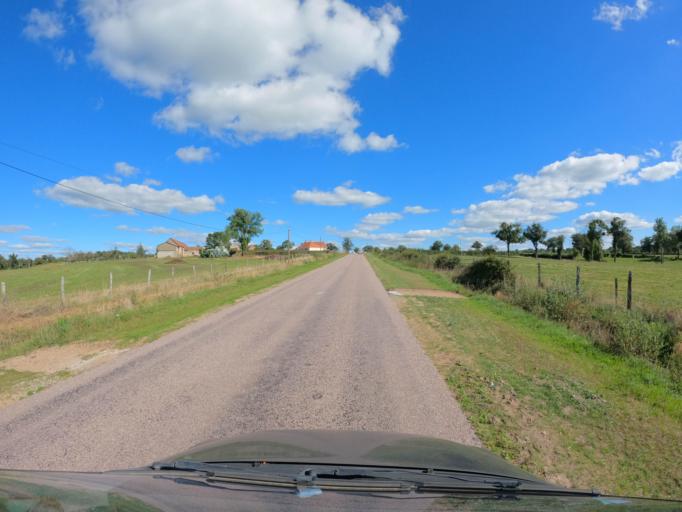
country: FR
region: Auvergne
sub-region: Departement de l'Allier
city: Buxieres-les-Mines
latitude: 46.4034
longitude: 3.0194
